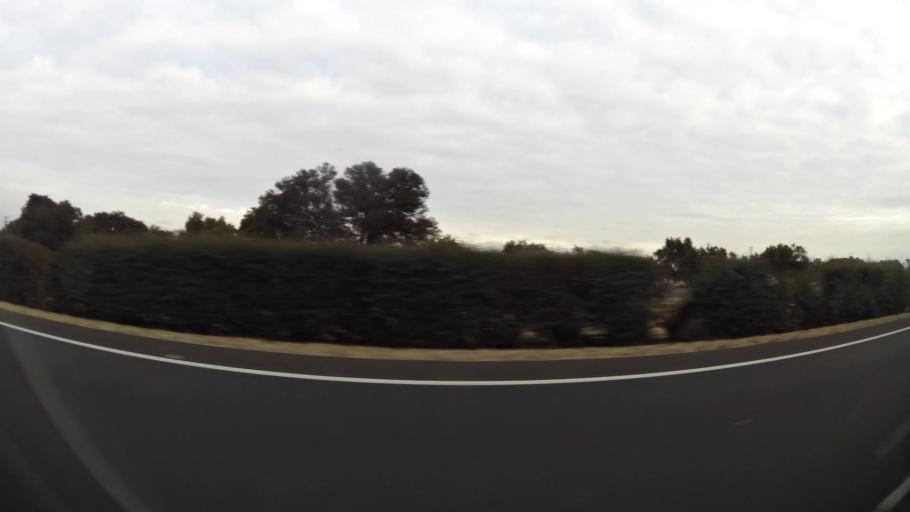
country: ZA
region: Orange Free State
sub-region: Mangaung Metropolitan Municipality
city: Bloemfontein
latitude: -29.1214
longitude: 26.1628
